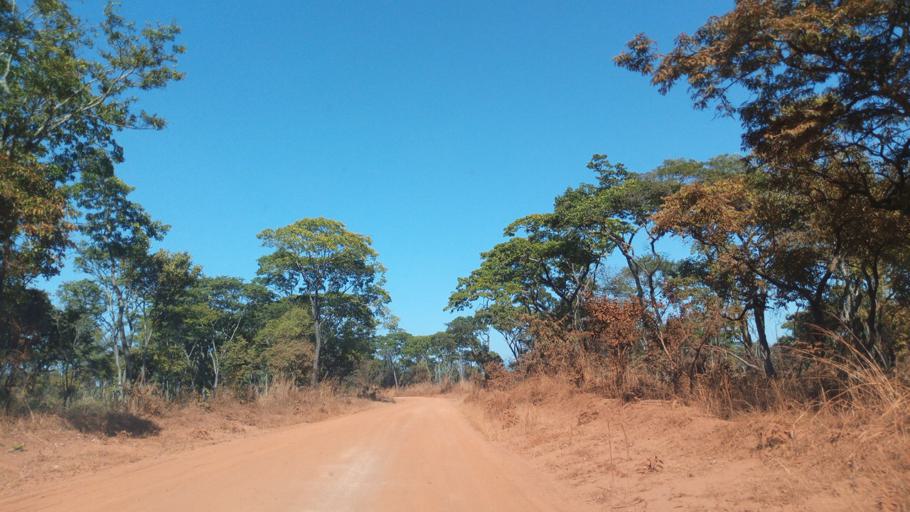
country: ZM
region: Luapula
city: Mwense
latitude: -10.6978
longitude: 28.3831
